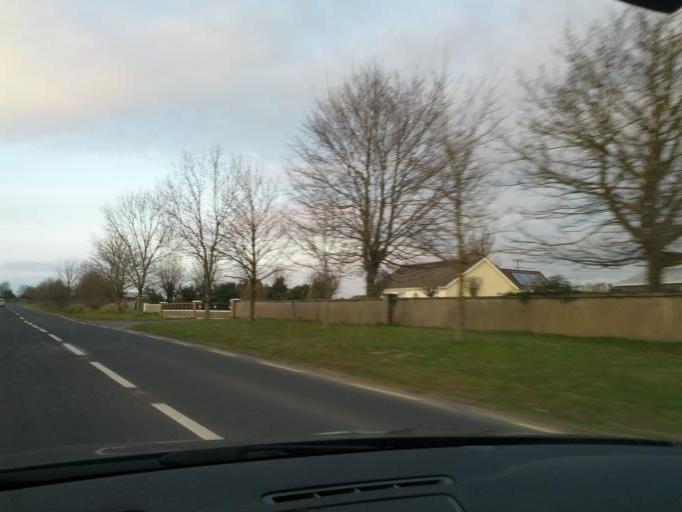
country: IE
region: Munster
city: Nenagh Bridge
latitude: 52.9028
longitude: -8.1849
